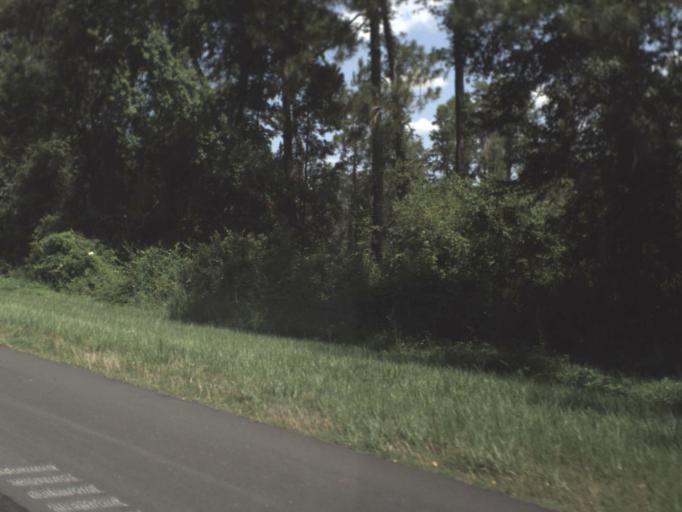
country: US
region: Florida
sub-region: Madison County
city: Madison
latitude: 30.4077
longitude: -83.4075
